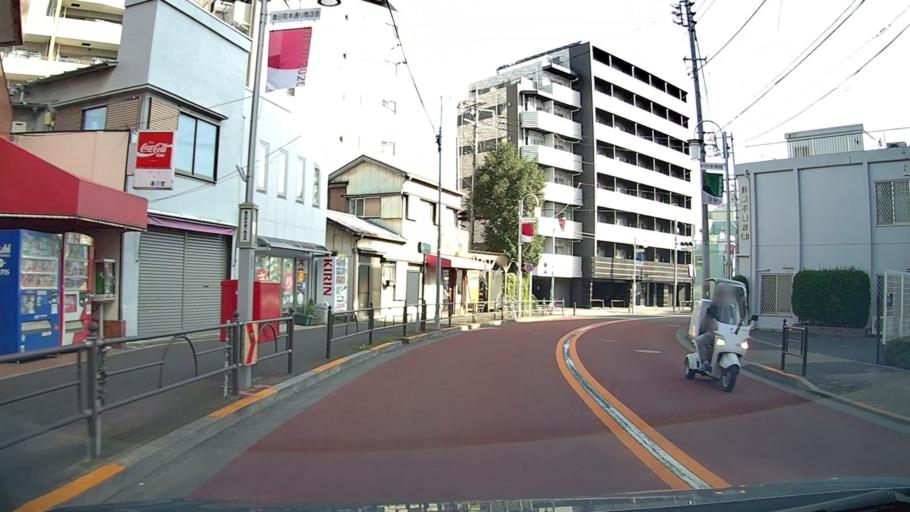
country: JP
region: Saitama
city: Wako
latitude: 35.7480
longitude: 139.6475
